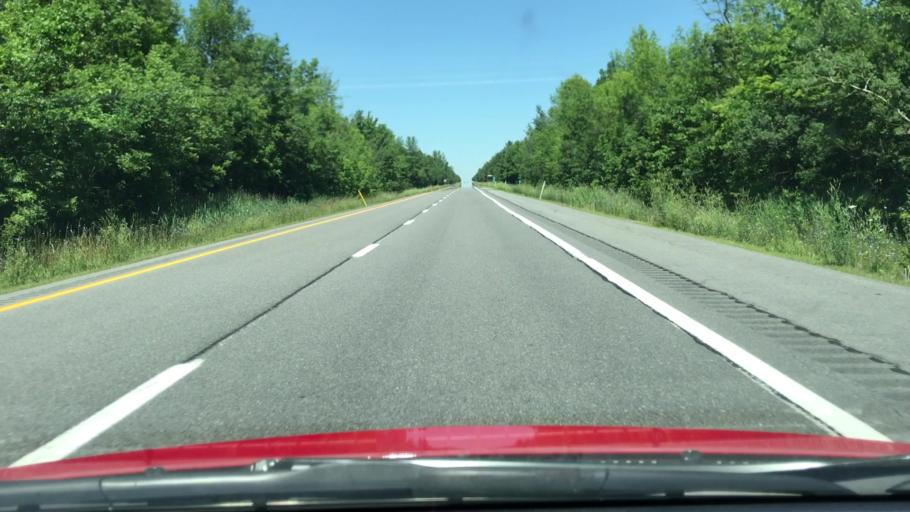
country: US
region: New York
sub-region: Clinton County
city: Champlain
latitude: 44.9498
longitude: -73.4481
